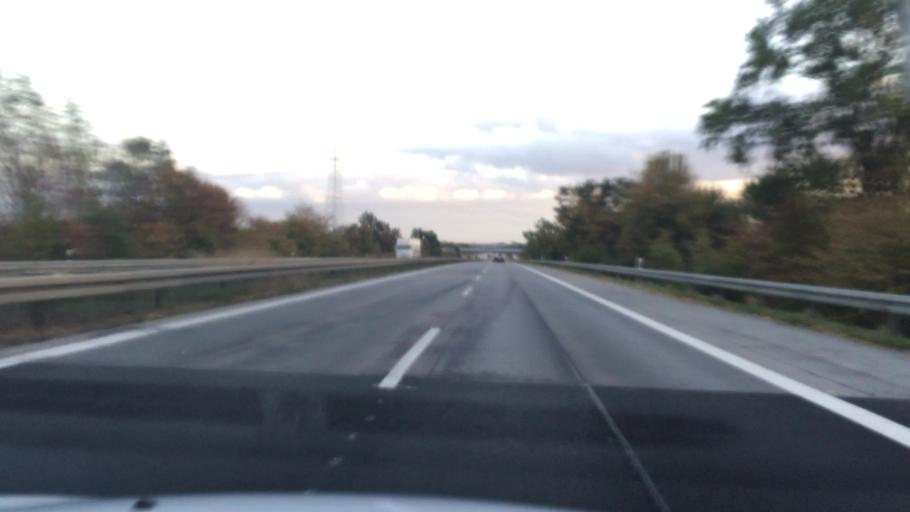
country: DE
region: Saxony
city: Borsdorf
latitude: 51.3423
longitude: 12.5077
